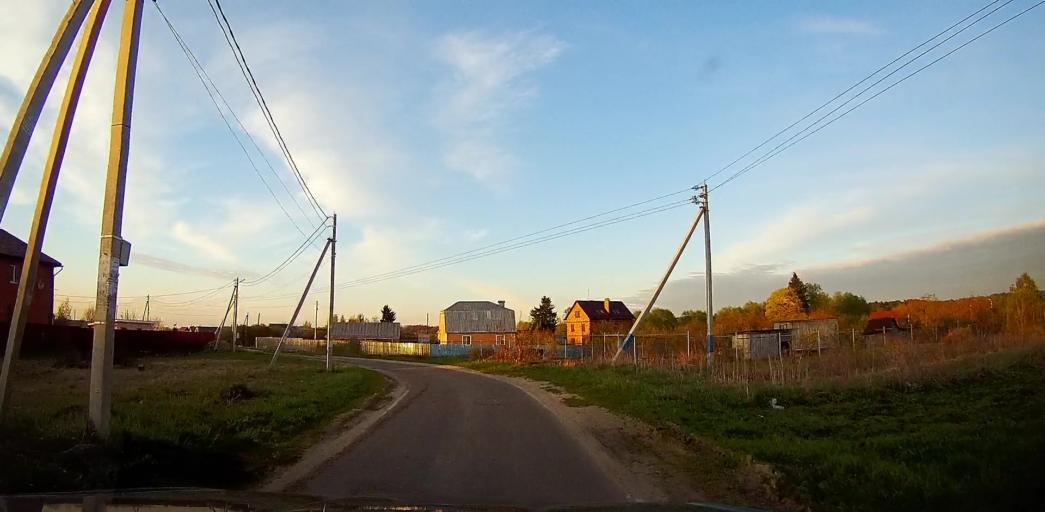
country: RU
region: Moskovskaya
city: Peski
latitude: 55.2103
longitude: 38.7401
